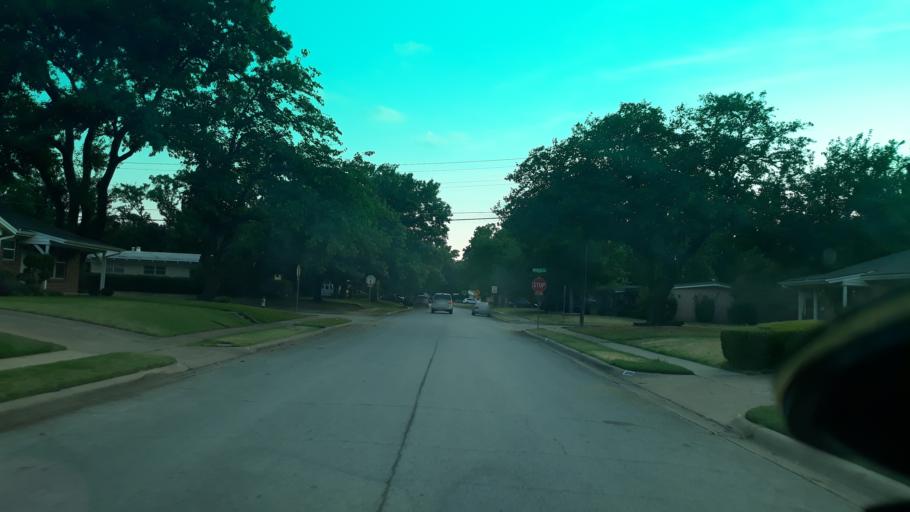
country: US
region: Texas
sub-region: Dallas County
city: Irving
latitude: 32.8347
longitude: -96.9804
